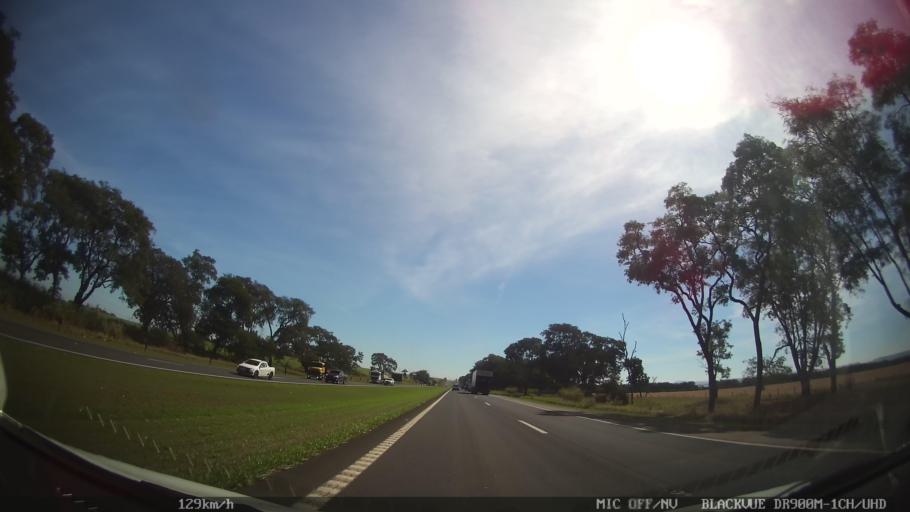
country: BR
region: Sao Paulo
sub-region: Porto Ferreira
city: Porto Ferreira
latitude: -21.8996
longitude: -47.4793
